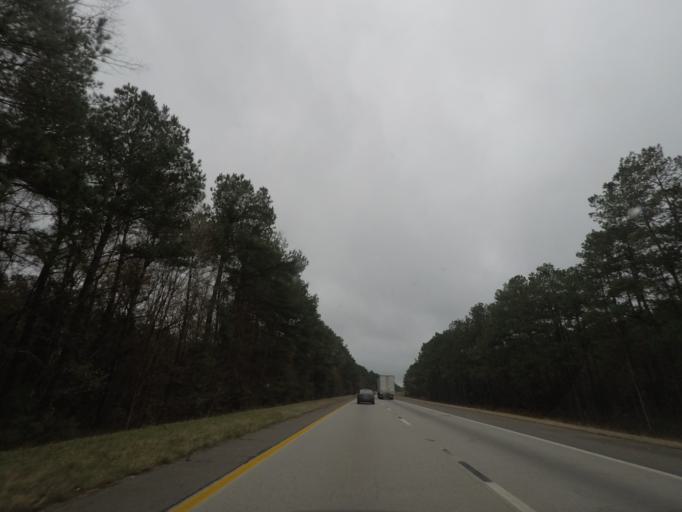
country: US
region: South Carolina
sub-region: Colleton County
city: Walterboro
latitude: 33.0201
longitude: -80.6661
